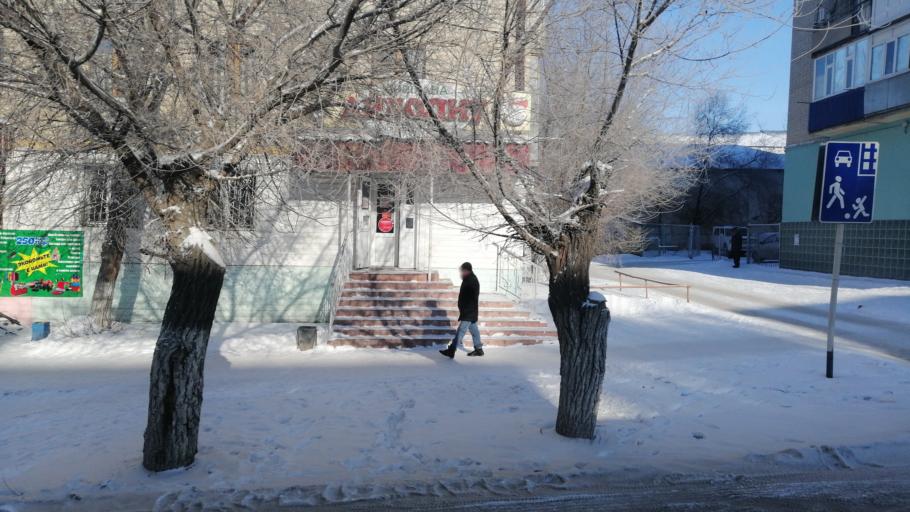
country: KZ
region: Aqtoebe
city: Aqtobe
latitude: 50.2814
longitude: 57.2220
